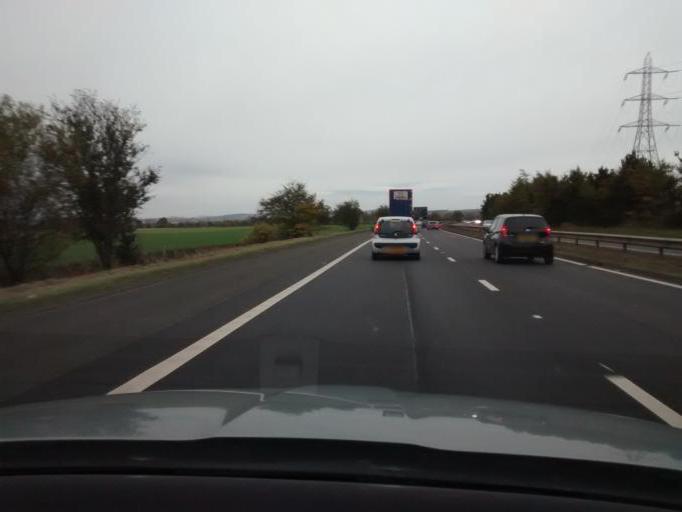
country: GB
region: Scotland
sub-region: Falkirk
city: Airth
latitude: 56.0373
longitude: -3.7706
